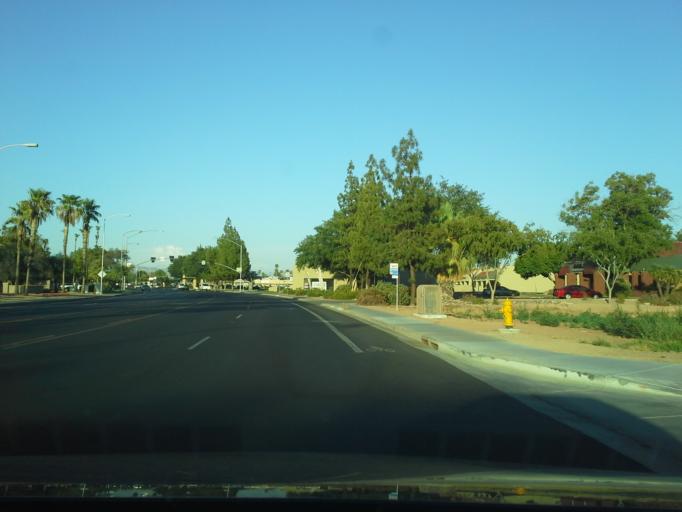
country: US
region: Arizona
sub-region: Maricopa County
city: Mesa
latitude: 33.4349
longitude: -111.8270
